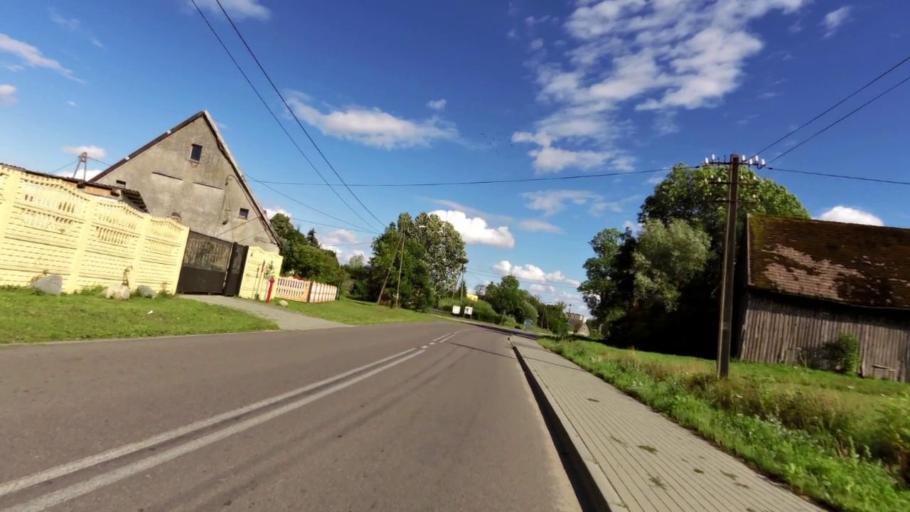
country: PL
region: West Pomeranian Voivodeship
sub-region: Powiat slawienski
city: Slawno
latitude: 54.4598
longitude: 16.7354
